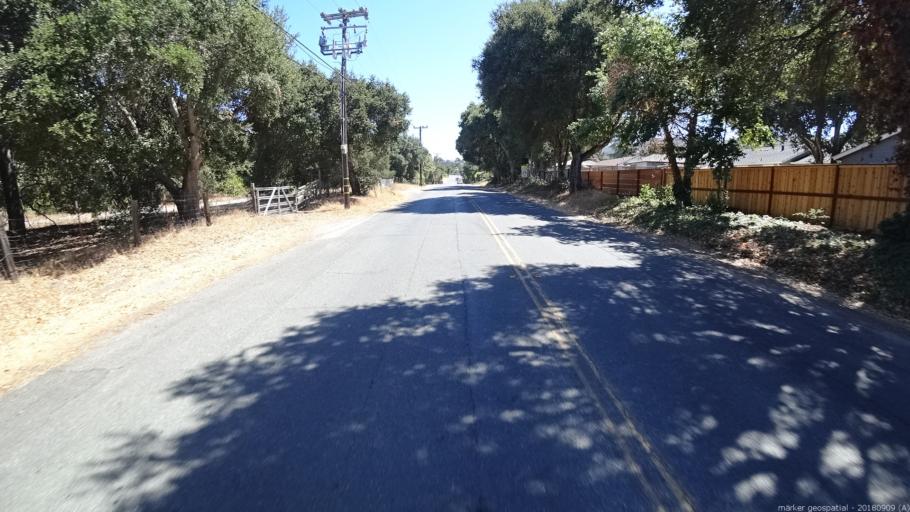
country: US
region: California
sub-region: Monterey County
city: Carmel Valley Village
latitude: 36.5782
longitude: -121.7193
